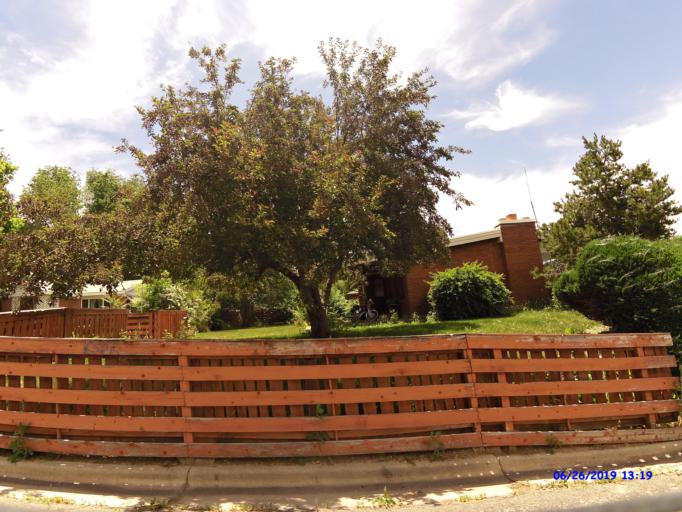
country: US
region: Utah
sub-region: Weber County
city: South Ogden
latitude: 41.2080
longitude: -111.9621
